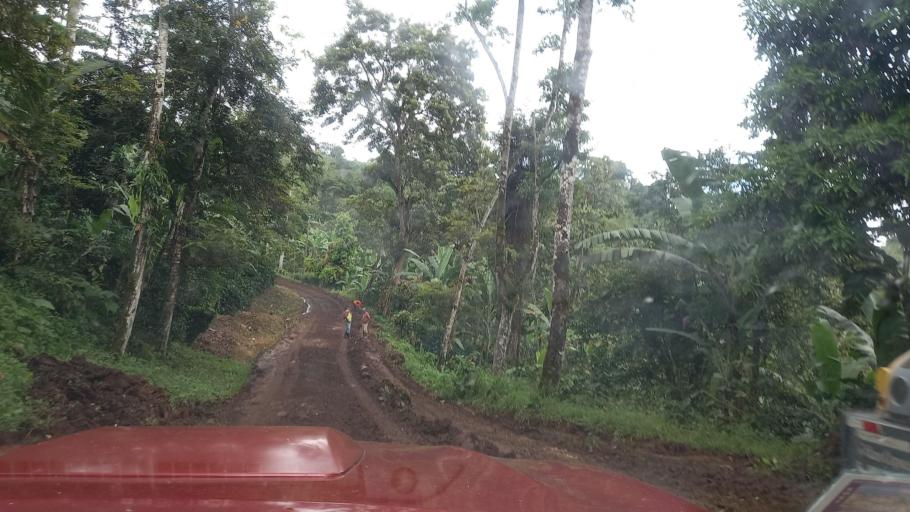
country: NI
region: Jinotega
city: San Jose de Bocay
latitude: 13.3421
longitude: -85.6544
